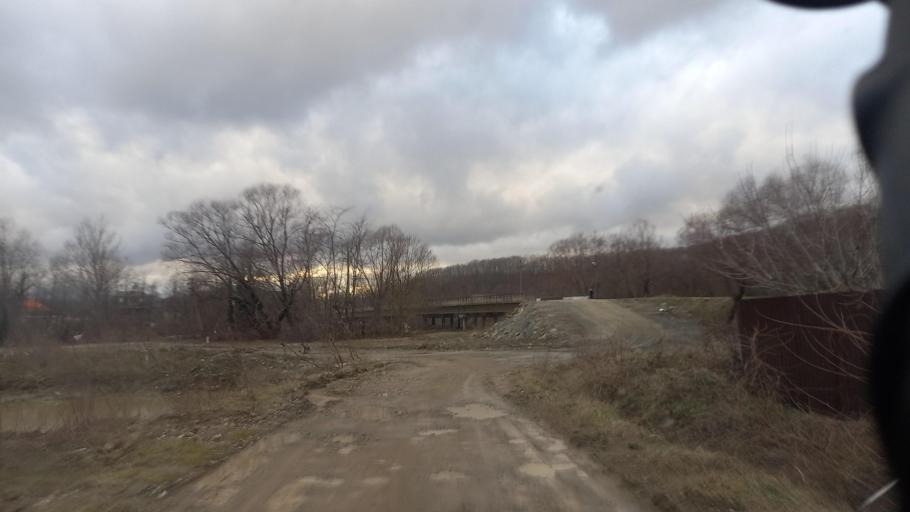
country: RU
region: Krasnodarskiy
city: Lermontovo
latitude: 44.4310
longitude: 38.7901
